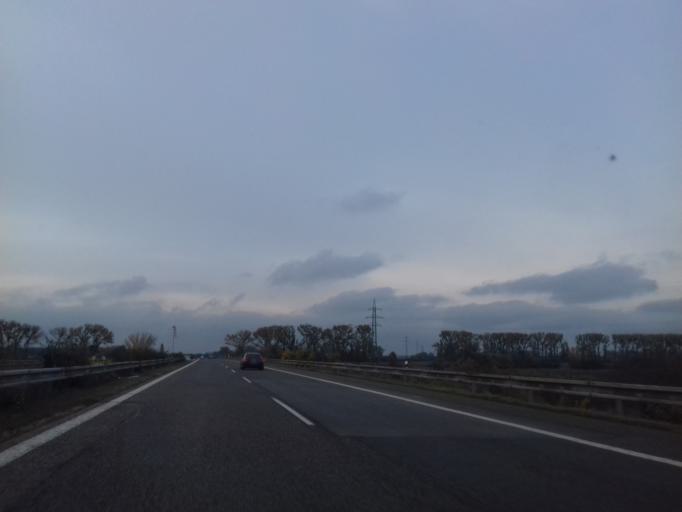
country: CZ
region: South Moravian
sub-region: Okres Breclav
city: Lanzhot
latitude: 48.6318
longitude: 17.0060
